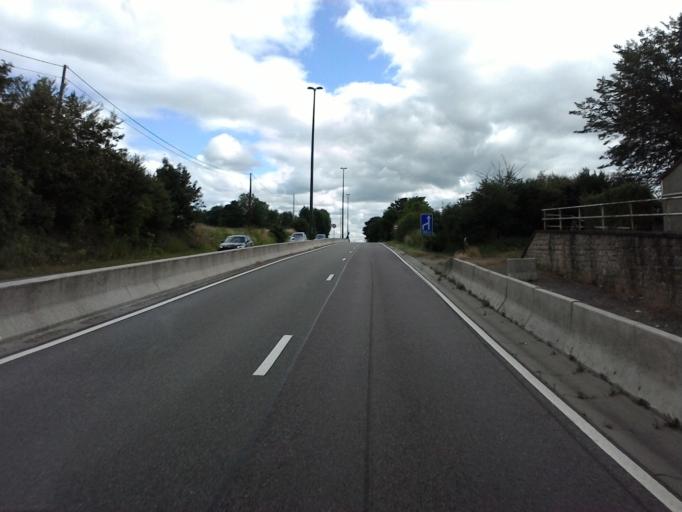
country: BE
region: Wallonia
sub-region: Province du Luxembourg
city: Arlon
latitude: 49.7159
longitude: 5.8016
